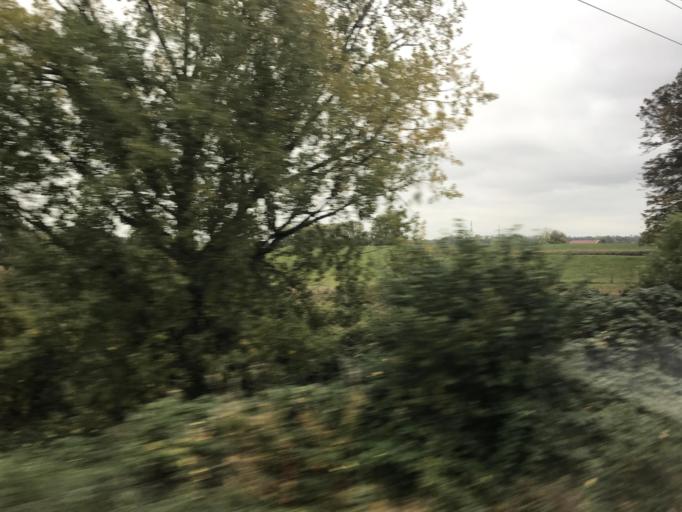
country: DE
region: Lower Saxony
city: Leer
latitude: 53.2133
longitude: 7.4652
